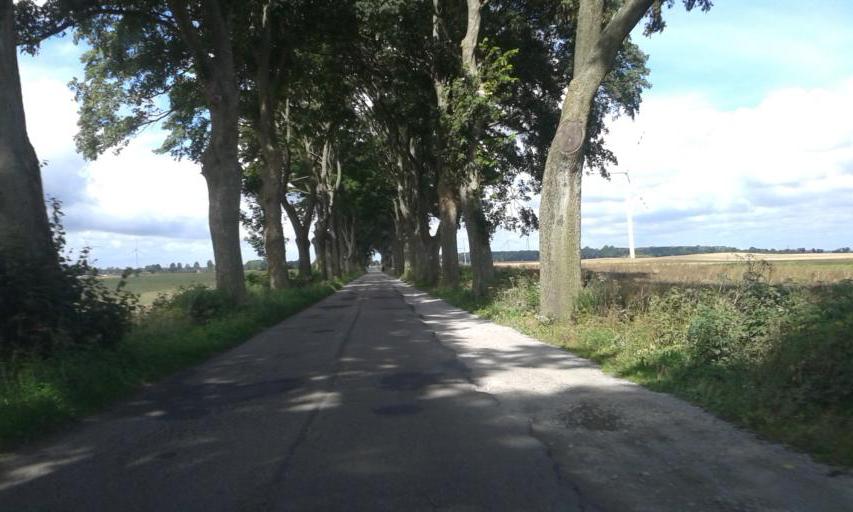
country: PL
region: West Pomeranian Voivodeship
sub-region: Powiat slawienski
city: Slawno
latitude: 54.3205
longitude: 16.5914
